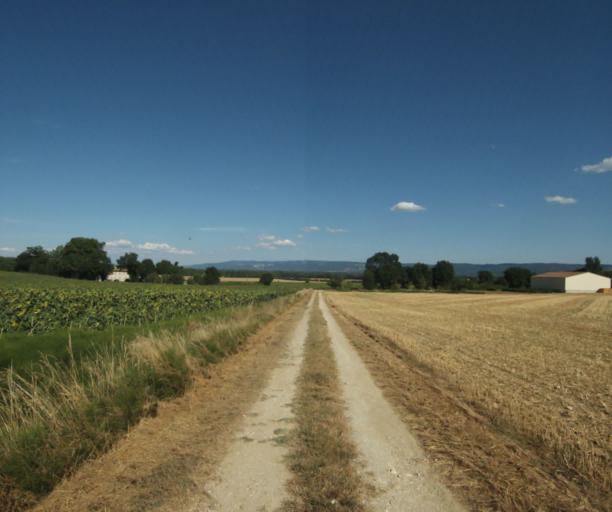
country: FR
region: Midi-Pyrenees
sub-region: Departement de la Haute-Garonne
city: Revel
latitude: 43.5007
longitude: 1.9434
